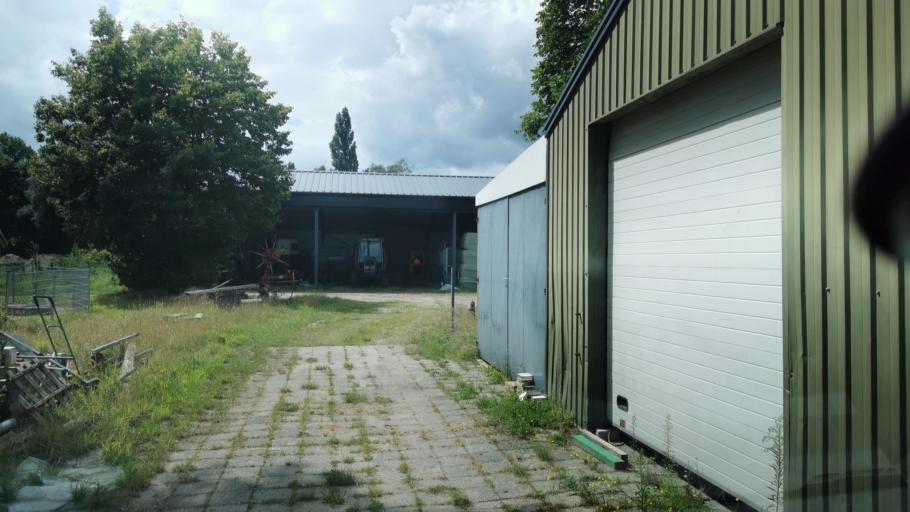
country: NL
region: Overijssel
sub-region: Gemeente Haaksbergen
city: Haaksbergen
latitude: 52.1614
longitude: 6.7634
